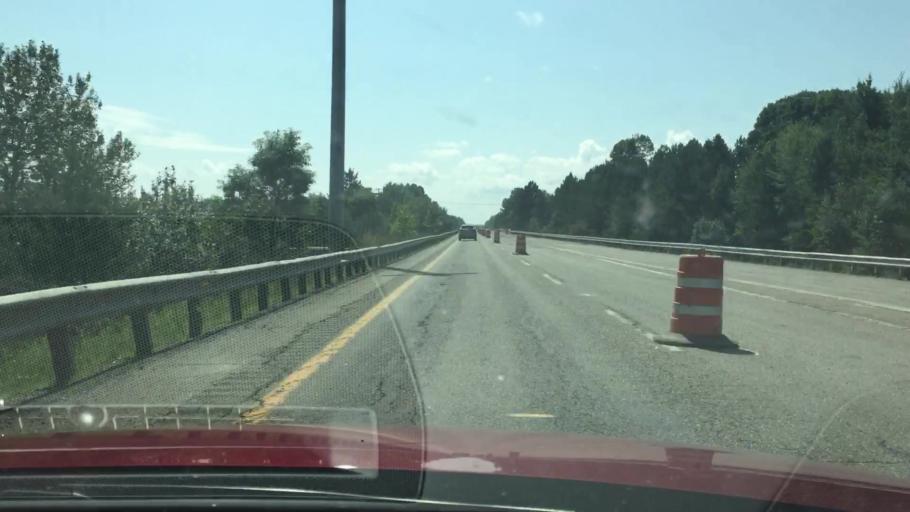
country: US
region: Maine
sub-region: Penobscot County
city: Patten
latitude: 45.8693
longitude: -68.4155
